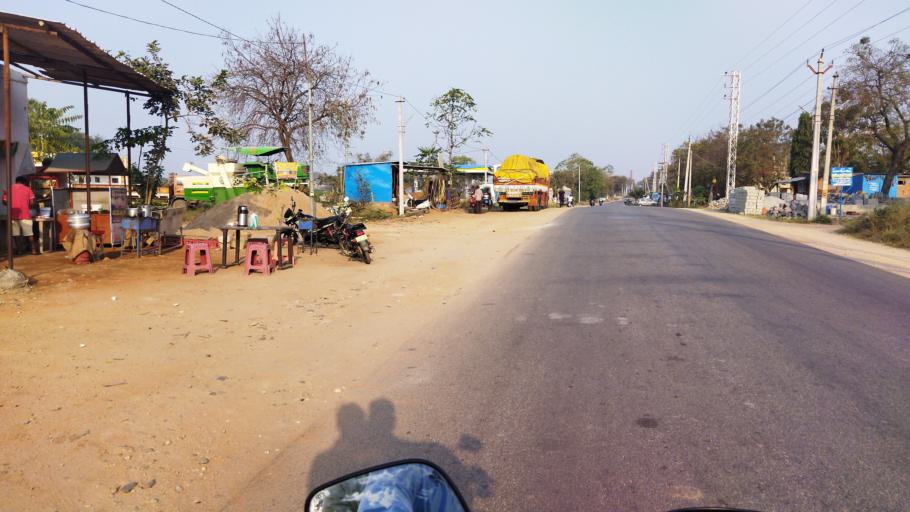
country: IN
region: Telangana
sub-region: Nalgonda
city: Nalgonda
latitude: 17.2360
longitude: 79.1216
